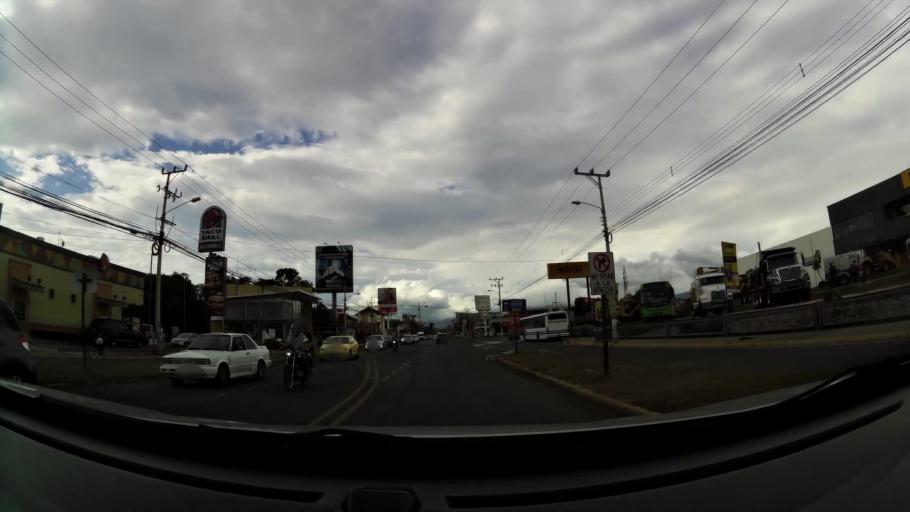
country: CR
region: San Jose
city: Santa Ana
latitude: 9.9514
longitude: -84.1936
